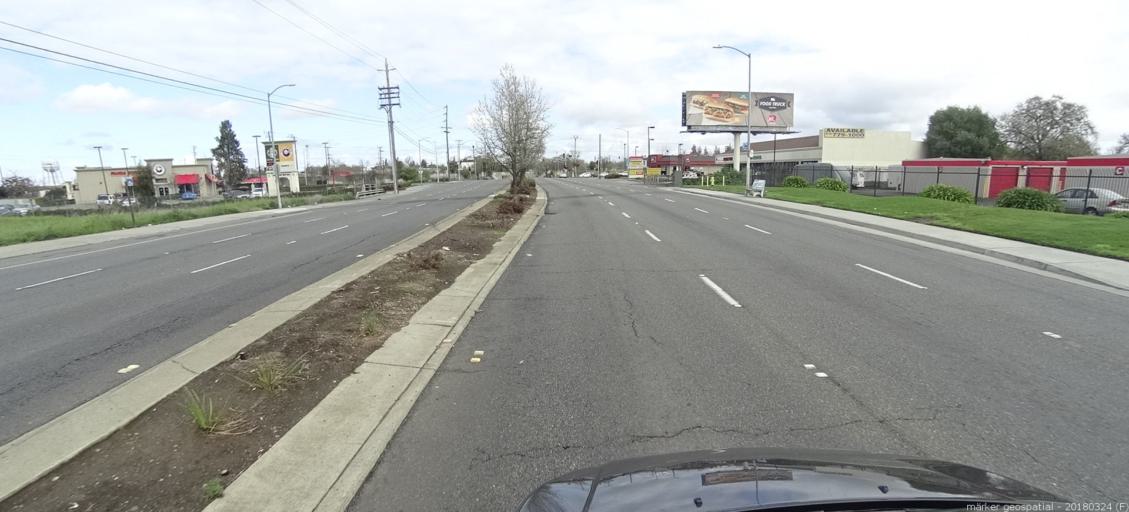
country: US
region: California
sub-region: Sacramento County
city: North Highlands
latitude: 38.6558
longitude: -121.3829
